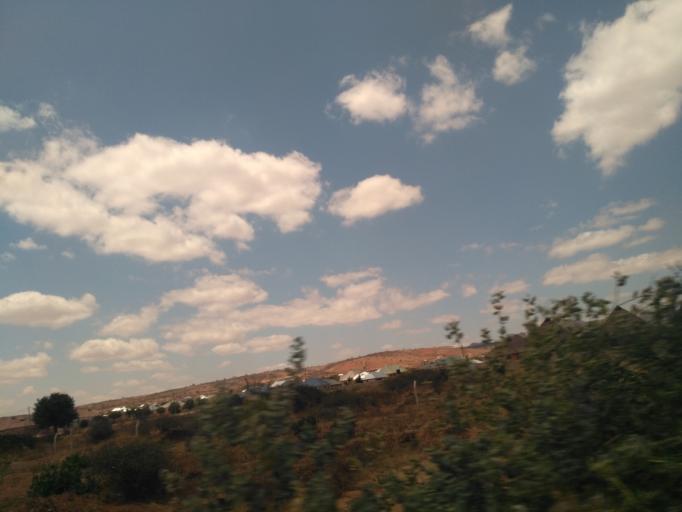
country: TZ
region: Dodoma
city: Kisasa
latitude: -6.1790
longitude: 35.7920
